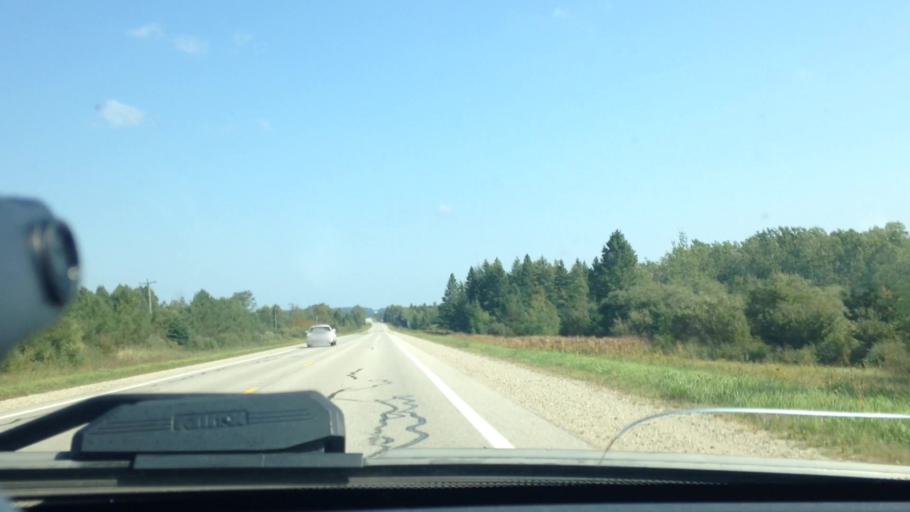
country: US
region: Michigan
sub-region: Luce County
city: Newberry
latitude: 46.3102
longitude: -85.6272
